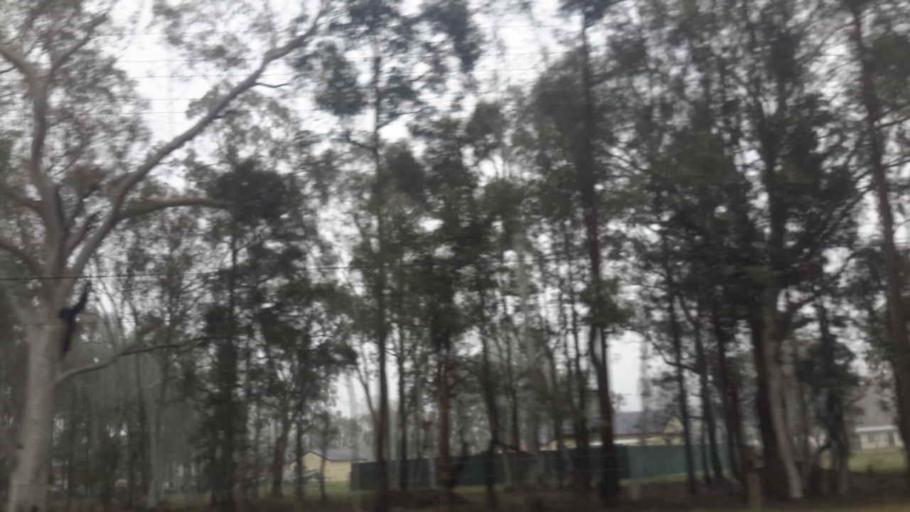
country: AU
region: New South Wales
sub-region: Hawkesbury
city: South Windsor
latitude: -33.6577
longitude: 150.7679
